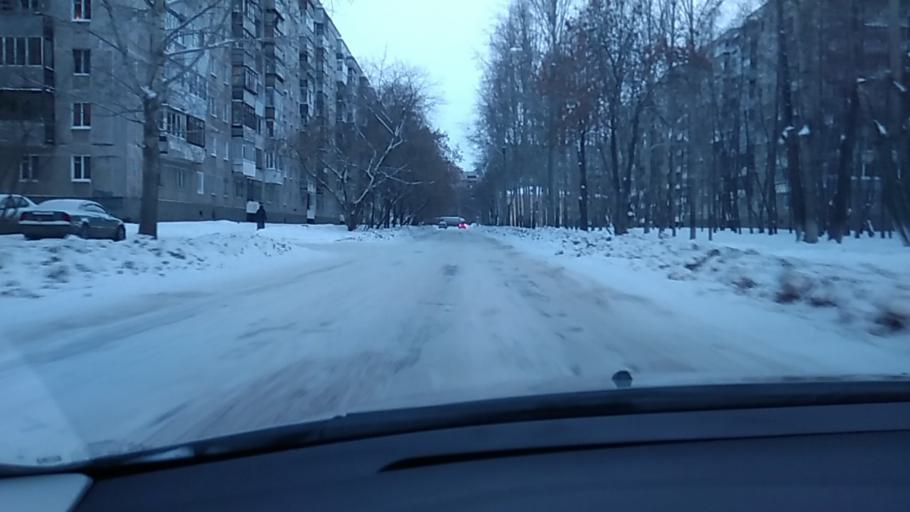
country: RU
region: Sverdlovsk
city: Yekaterinburg
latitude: 56.8952
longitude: 60.5991
